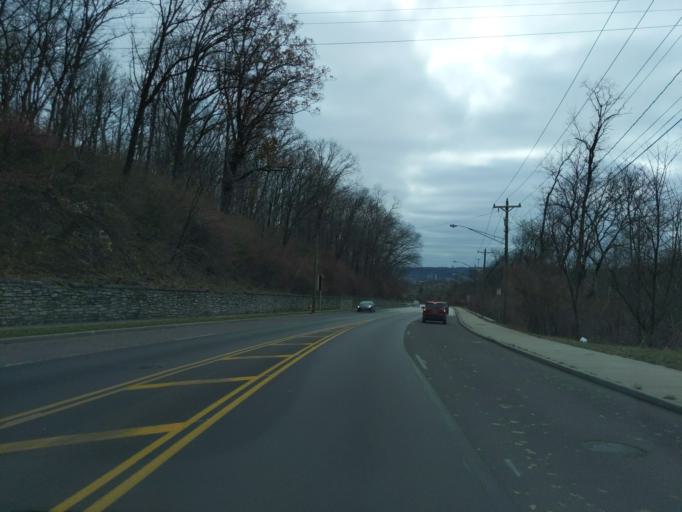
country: US
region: Ohio
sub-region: Hamilton County
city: Finneytown
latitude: 39.1845
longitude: -84.5443
